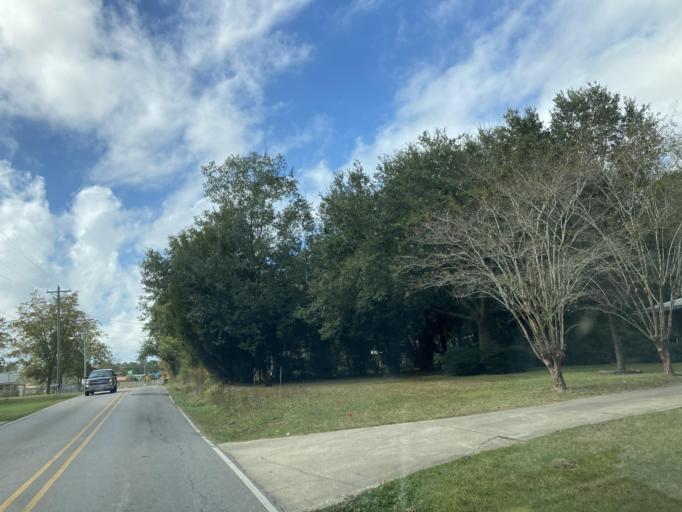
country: US
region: Mississippi
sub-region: Jackson County
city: Gulf Hills
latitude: 30.4391
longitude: -88.8312
